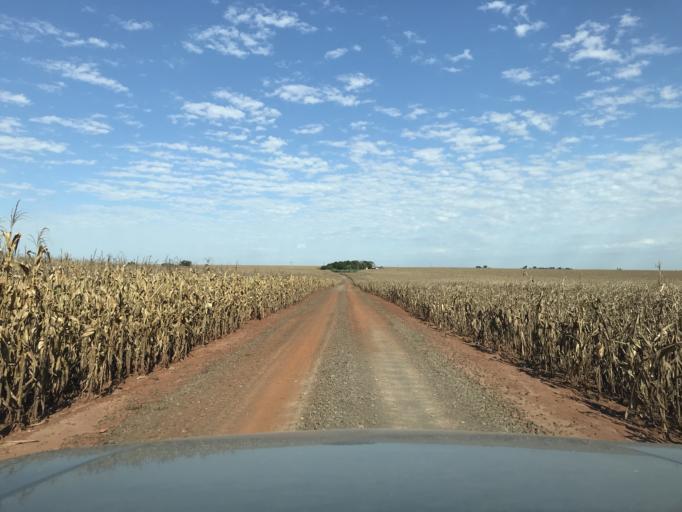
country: BR
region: Parana
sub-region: Palotina
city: Palotina
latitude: -24.1698
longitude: -53.7570
